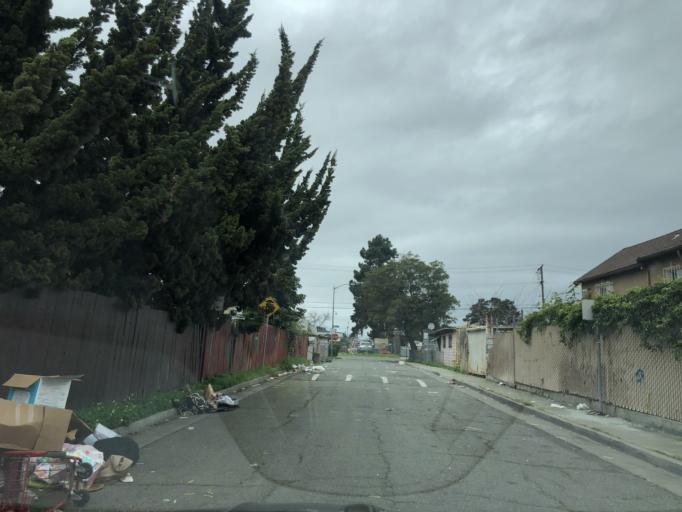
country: US
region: California
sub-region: Alameda County
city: San Leandro
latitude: 37.7456
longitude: -122.1800
